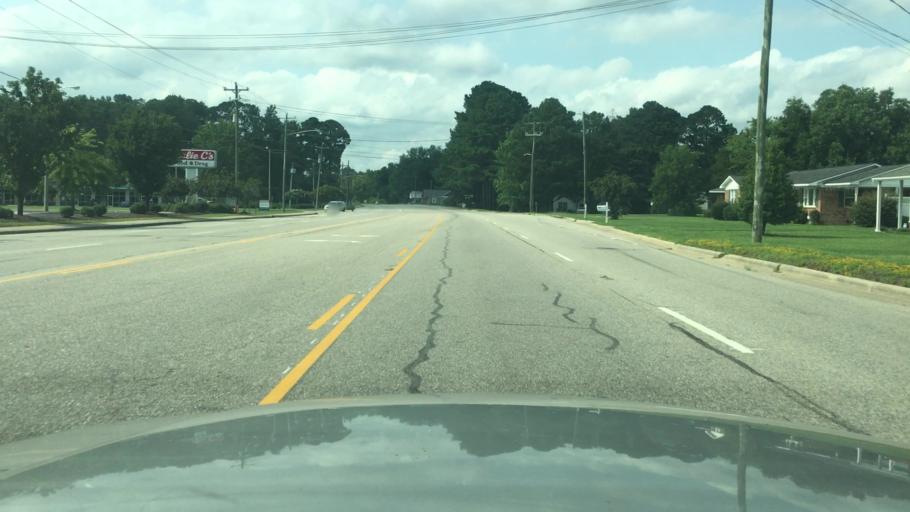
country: US
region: North Carolina
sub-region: Cumberland County
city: Fayetteville
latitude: 35.0352
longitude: -78.8459
